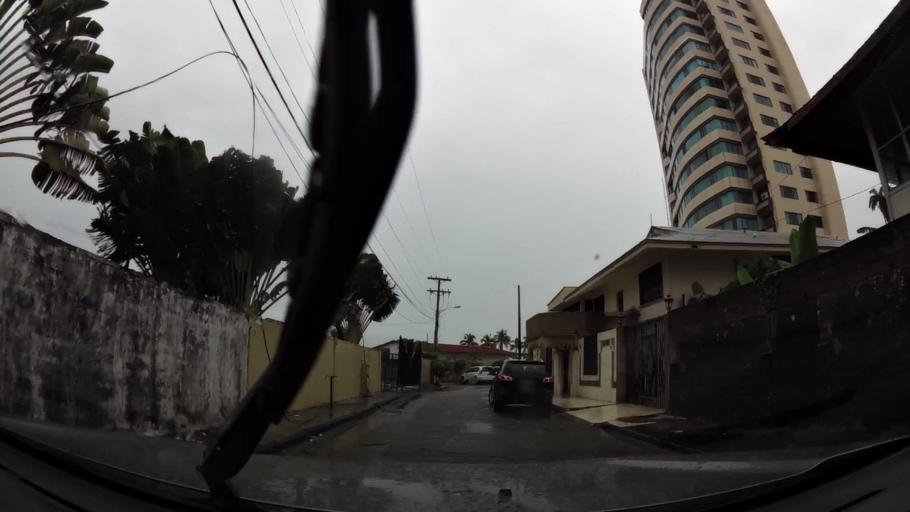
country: PA
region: Colon
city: Colon
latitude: 9.3638
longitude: -79.9075
